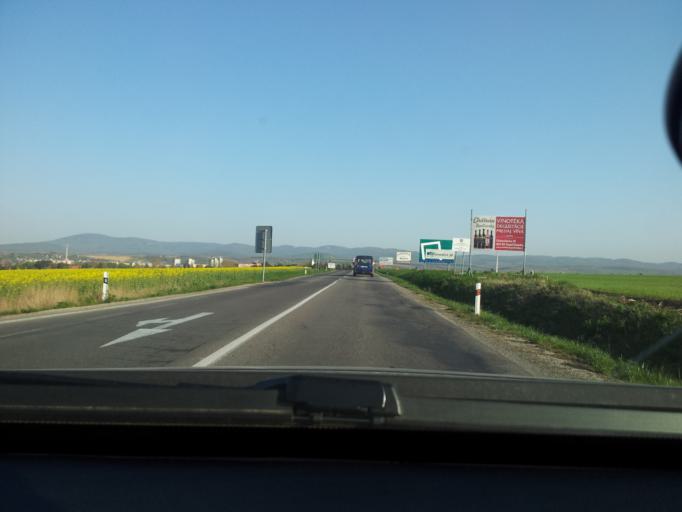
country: SK
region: Nitriansky
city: Zlate Moravce
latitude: 48.3744
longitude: 18.4048
